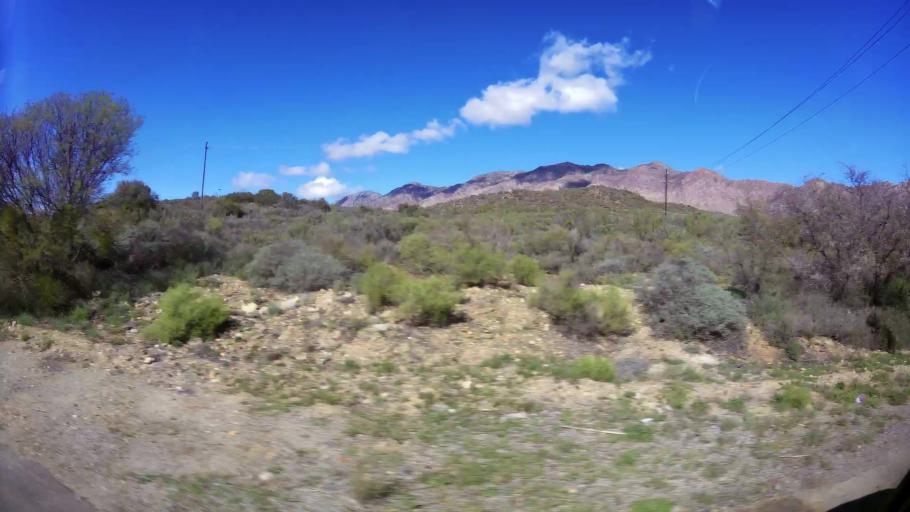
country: ZA
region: Western Cape
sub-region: Cape Winelands District Municipality
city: Ashton
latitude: -33.7890
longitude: 20.1333
